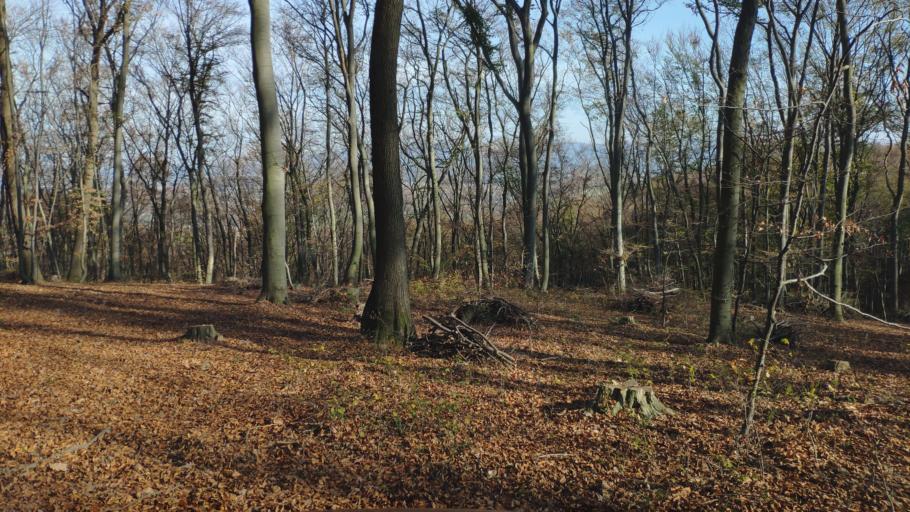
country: SK
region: Presovsky
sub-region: Okres Presov
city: Presov
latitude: 48.8961
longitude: 21.2286
